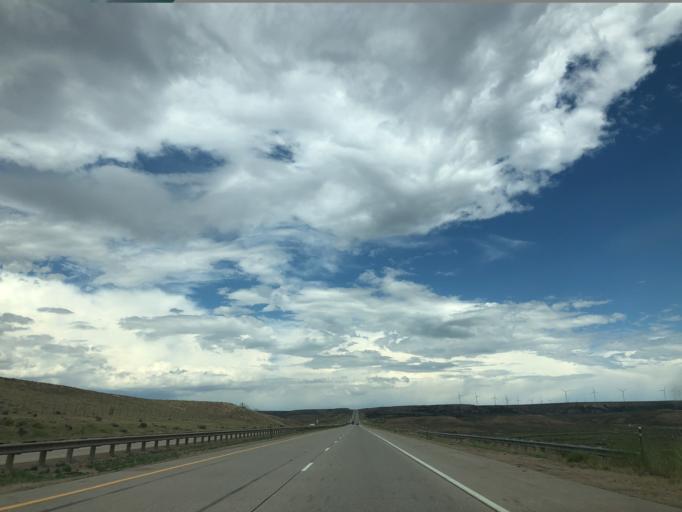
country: US
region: Wyoming
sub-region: Uinta County
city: Mountain View
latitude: 41.2982
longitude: -110.6155
